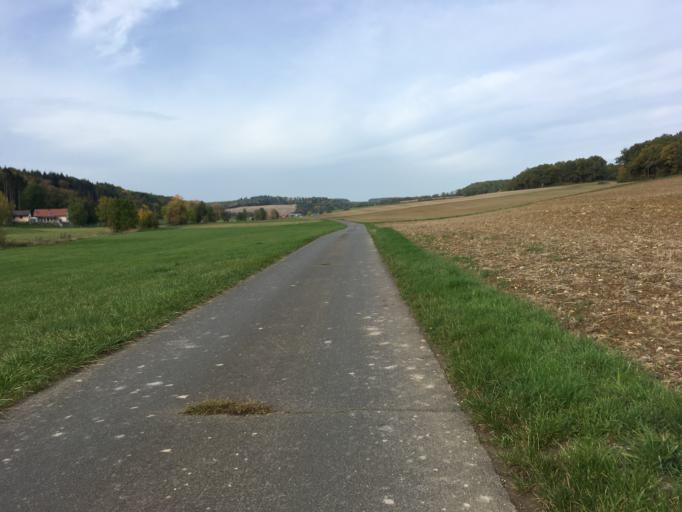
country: DE
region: Baden-Wuerttemberg
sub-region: Karlsruhe Region
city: Rosenberg
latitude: 49.4758
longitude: 9.4682
